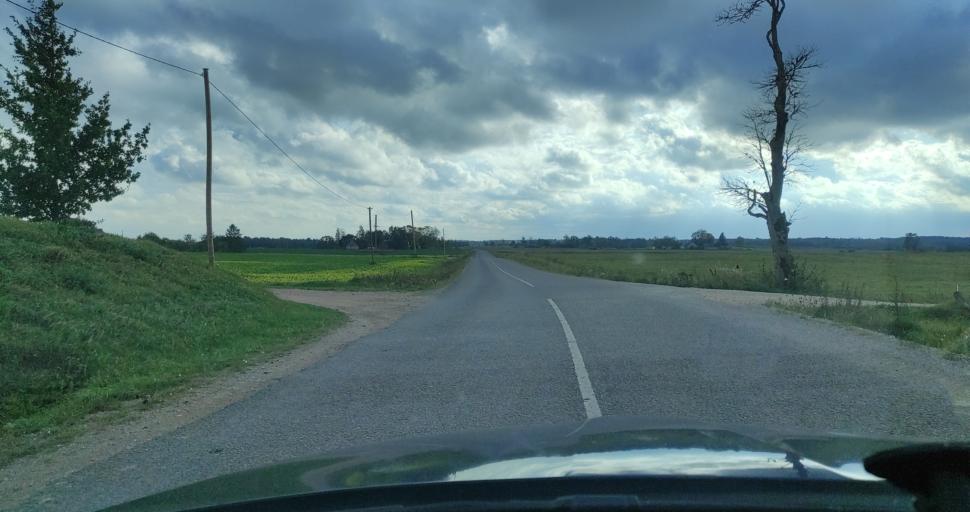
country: LV
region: Talsu Rajons
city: Sabile
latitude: 56.9415
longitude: 22.3965
